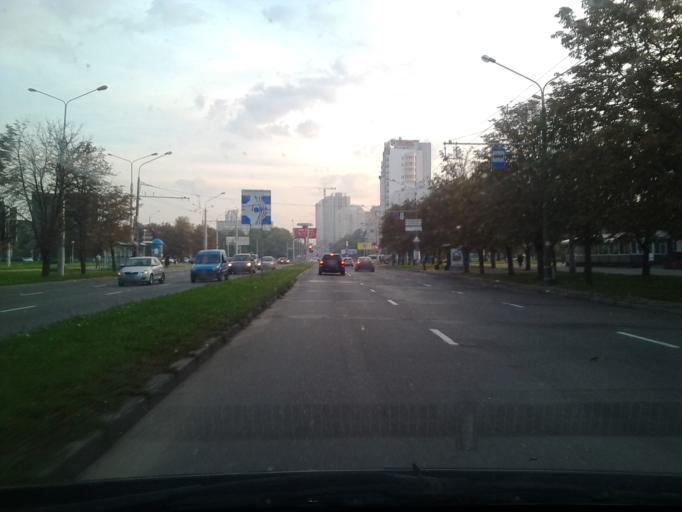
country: BY
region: Minsk
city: Minsk
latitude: 53.9297
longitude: 27.5753
